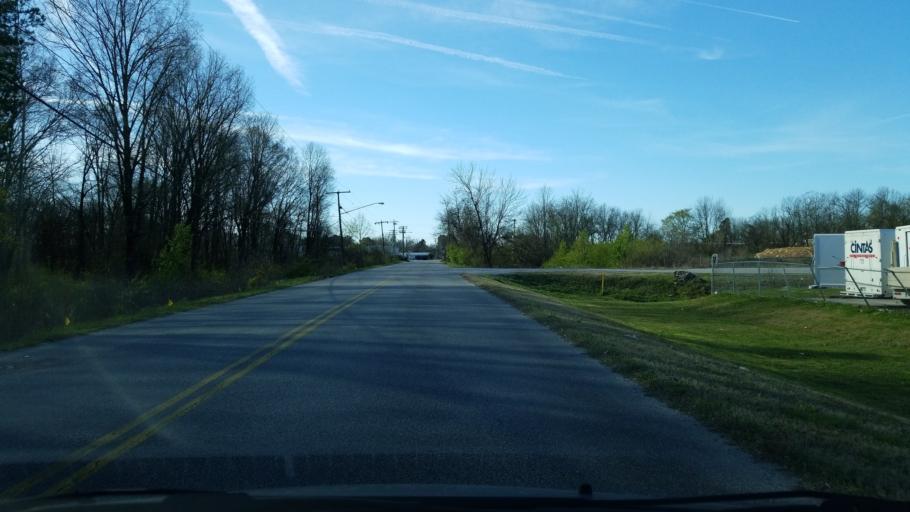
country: US
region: Tennessee
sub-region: Hamilton County
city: East Chattanooga
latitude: 35.0487
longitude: -85.1935
